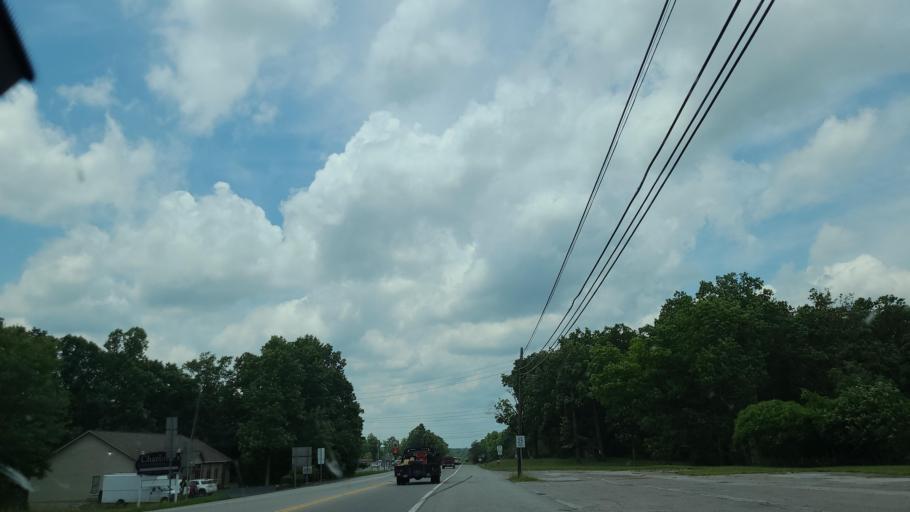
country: US
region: Tennessee
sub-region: Cumberland County
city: Crossville
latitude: 35.9056
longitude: -84.9856
